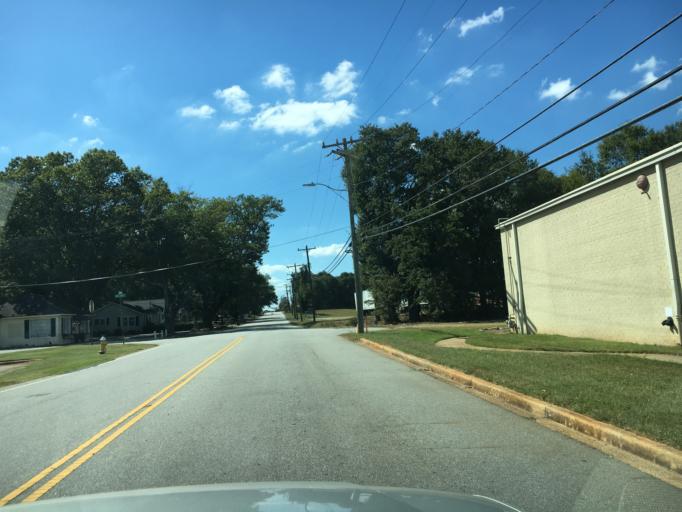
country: US
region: South Carolina
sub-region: Greenville County
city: Greenville
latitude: 34.8440
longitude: -82.3560
